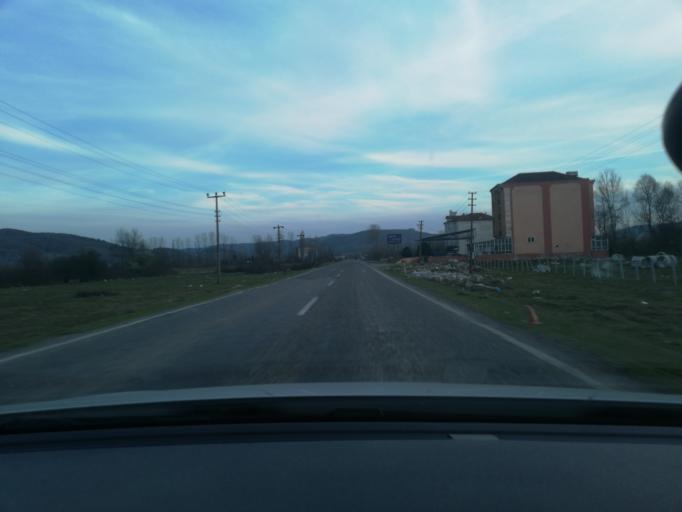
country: TR
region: Zonguldak
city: Saltukova
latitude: 41.5198
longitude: 32.1020
